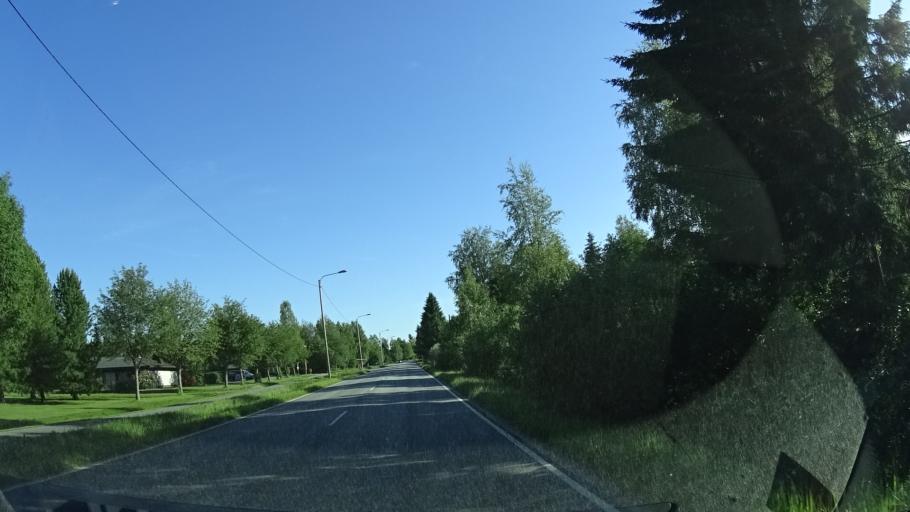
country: FI
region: Satakunta
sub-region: Pori
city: Ulvila
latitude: 61.4528
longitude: 21.8922
